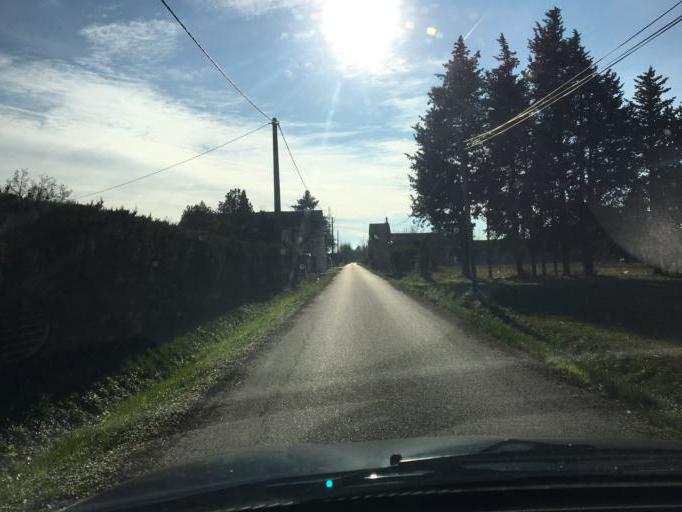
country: FR
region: Provence-Alpes-Cote d'Azur
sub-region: Departement du Vaucluse
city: Jonquieres
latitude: 44.1132
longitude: 4.8863
